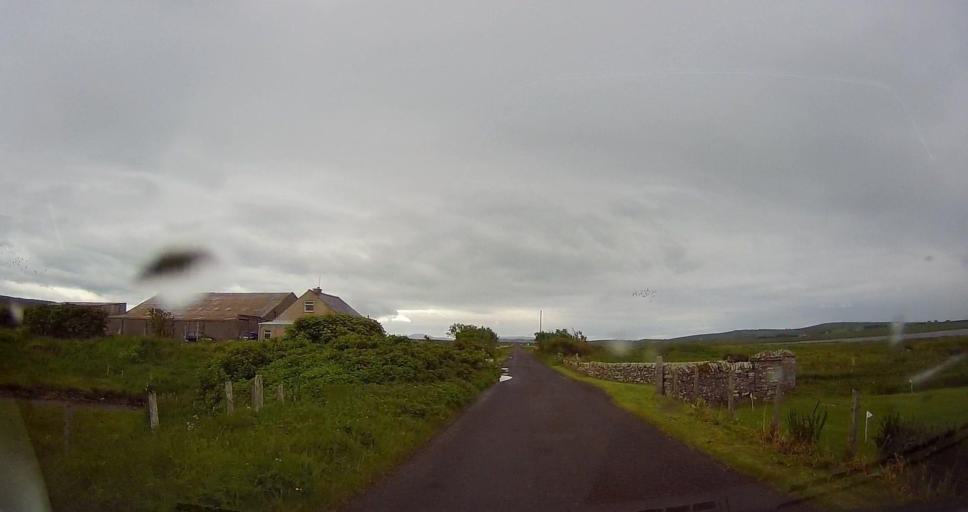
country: GB
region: Scotland
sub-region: Orkney Islands
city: Stromness
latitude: 59.1095
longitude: -3.2531
